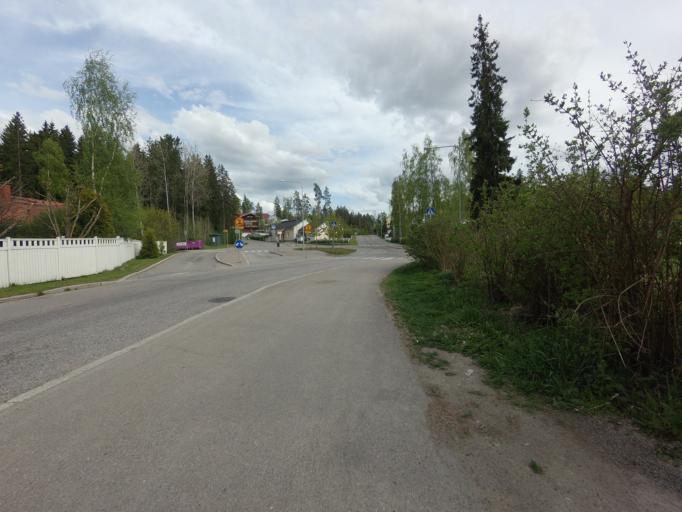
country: FI
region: Uusimaa
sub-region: Helsinki
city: Kauniainen
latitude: 60.1974
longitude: 24.7181
